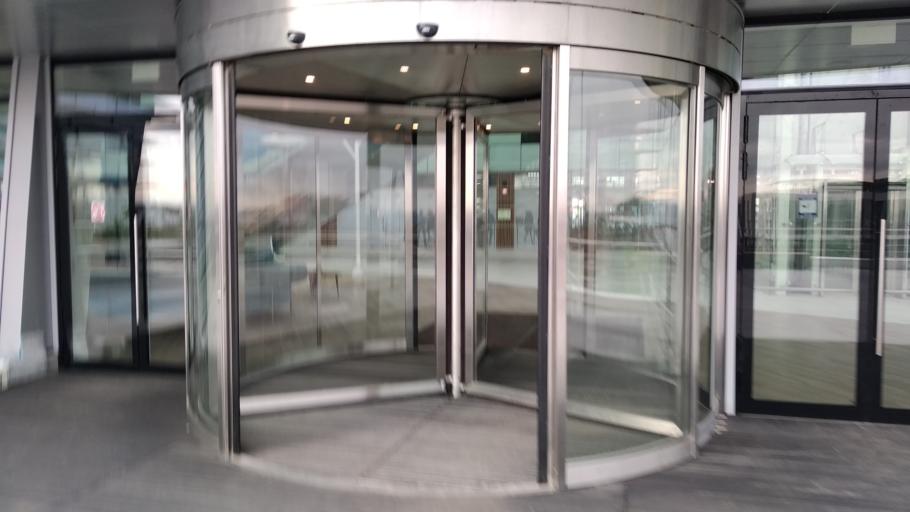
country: RU
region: Moskovskaya
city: Novoivanovskoye
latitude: 55.6964
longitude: 37.3474
